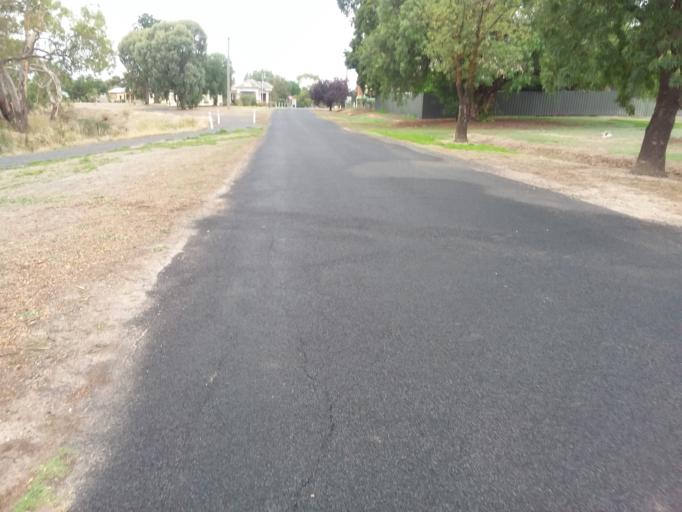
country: AU
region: Victoria
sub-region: Horsham
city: Horsham
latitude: -36.7411
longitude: 141.9404
